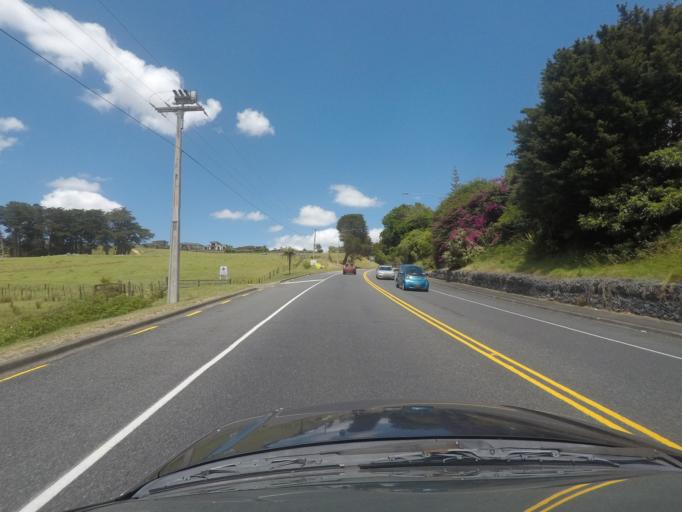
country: NZ
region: Northland
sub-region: Whangarei
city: Whangarei
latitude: -35.7422
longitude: 174.3650
